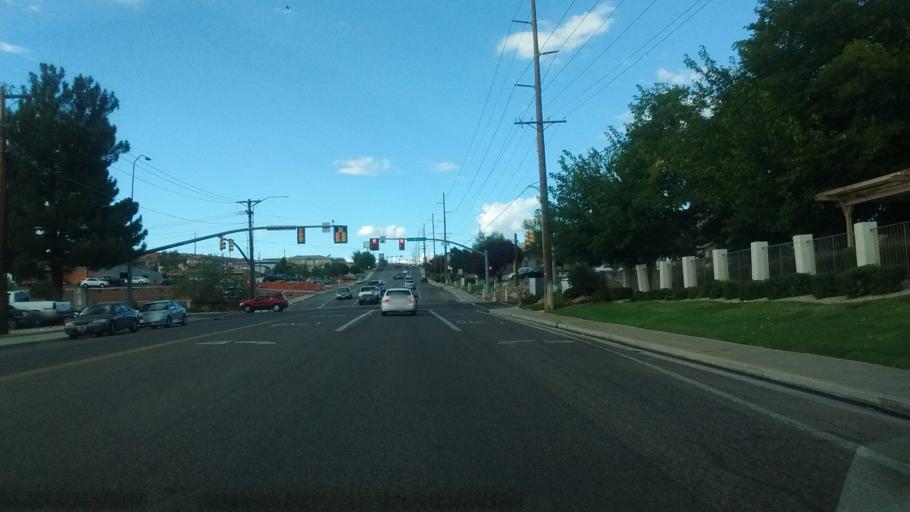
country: US
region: Utah
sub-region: Washington County
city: Saint George
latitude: 37.1058
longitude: -113.5621
